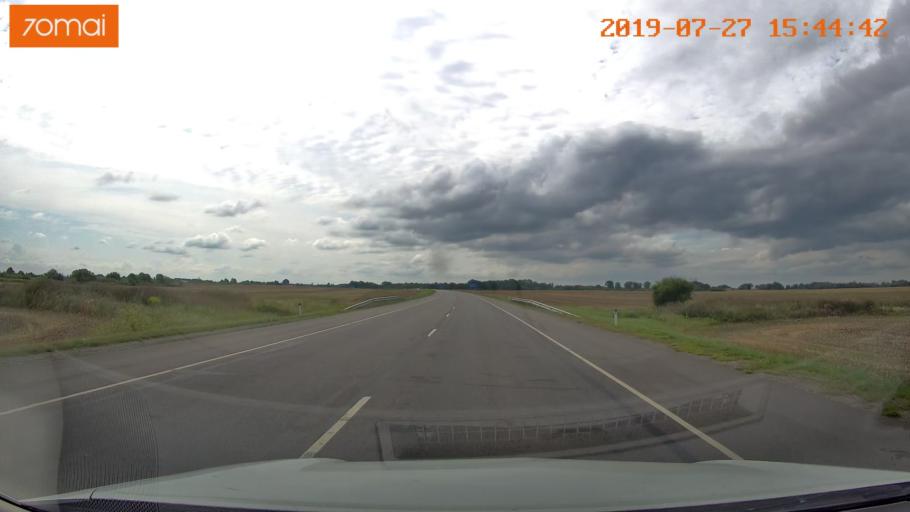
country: RU
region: Kaliningrad
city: Gusev
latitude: 54.6149
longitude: 22.1575
